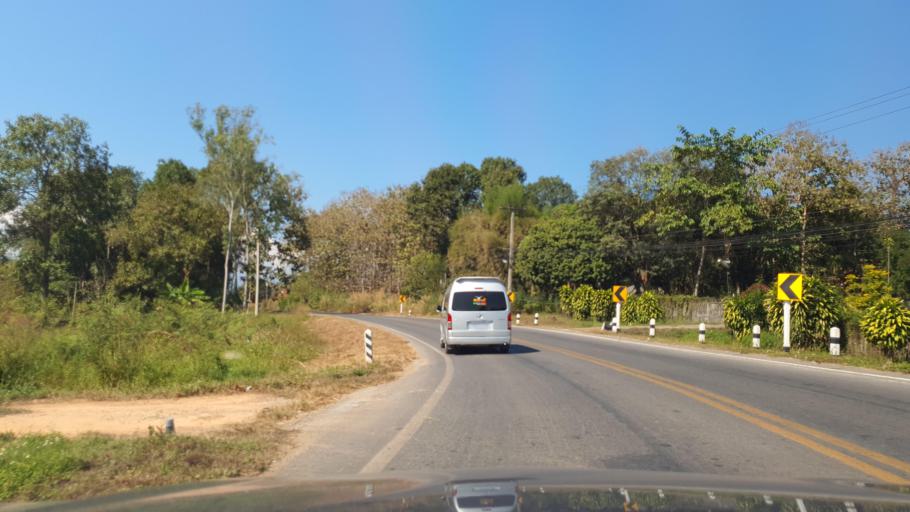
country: TH
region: Nan
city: Tha Wang Pha
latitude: 19.1023
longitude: 100.8247
